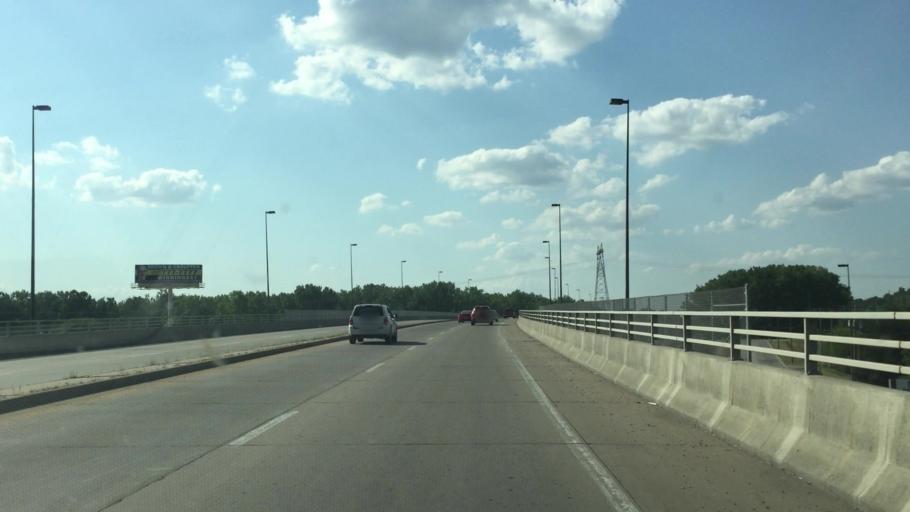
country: US
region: Missouri
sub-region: Clay County
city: North Kansas City
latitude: 39.1387
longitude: -94.5297
